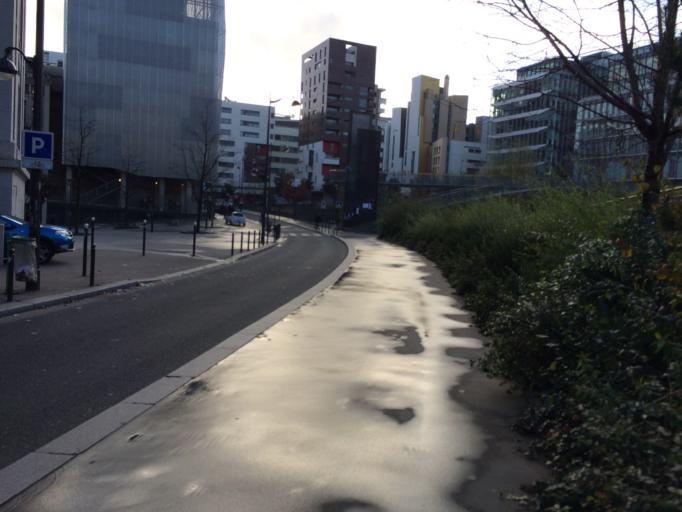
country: FR
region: Ile-de-France
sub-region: Departement du Val-de-Marne
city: Ivry-sur-Seine
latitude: 48.8297
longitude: 2.3804
